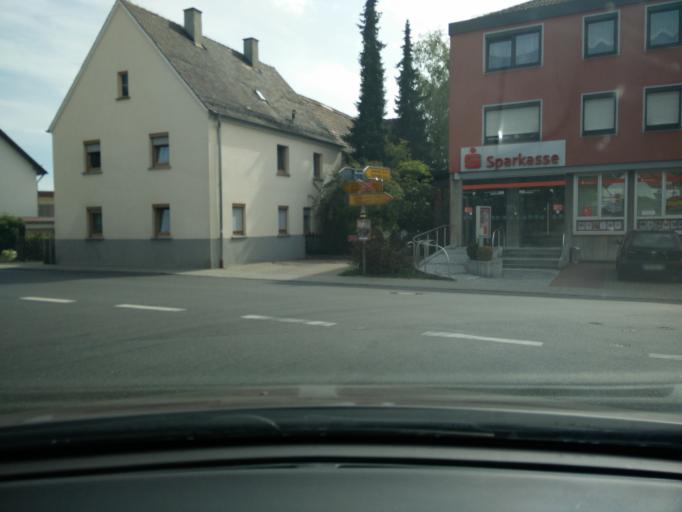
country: DE
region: Bavaria
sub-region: Regierungsbezirk Mittelfranken
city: Veitsbronn
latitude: 49.5118
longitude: 10.8826
